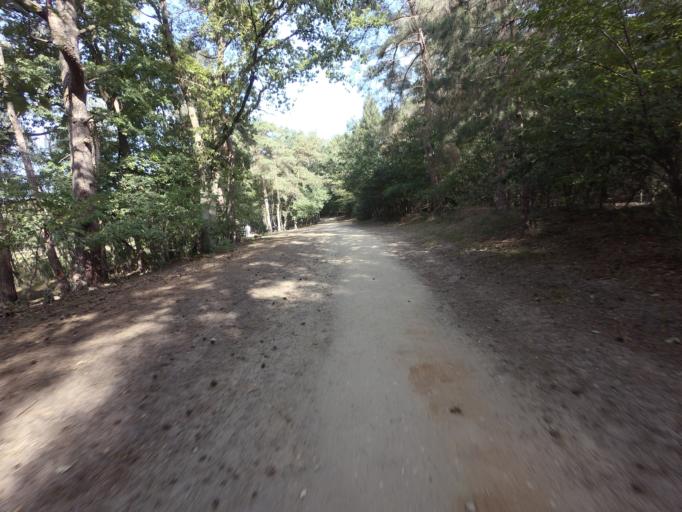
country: NL
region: Limburg
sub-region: Gemeente Roerdalen
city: Herkenbosch
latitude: 51.1758
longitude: 6.0802
